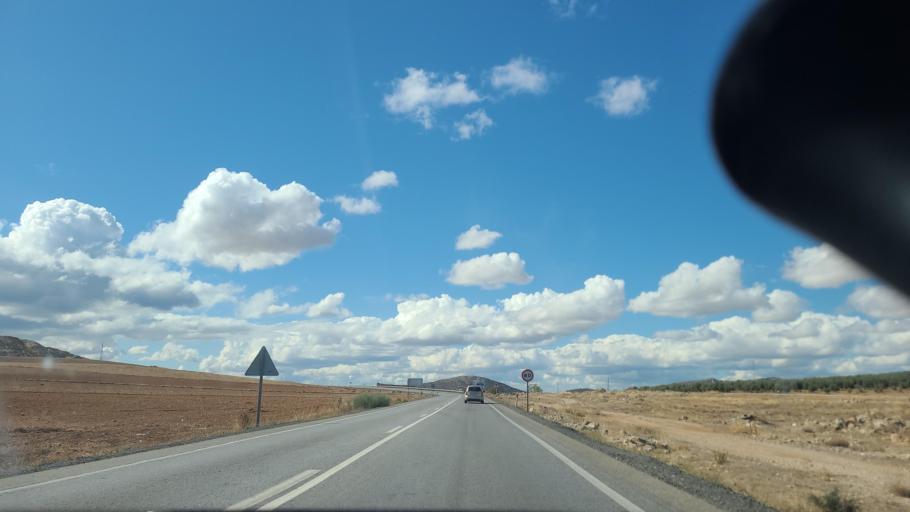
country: ES
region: Andalusia
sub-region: Provincia de Granada
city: Gobernador
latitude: 37.4120
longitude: -3.3582
